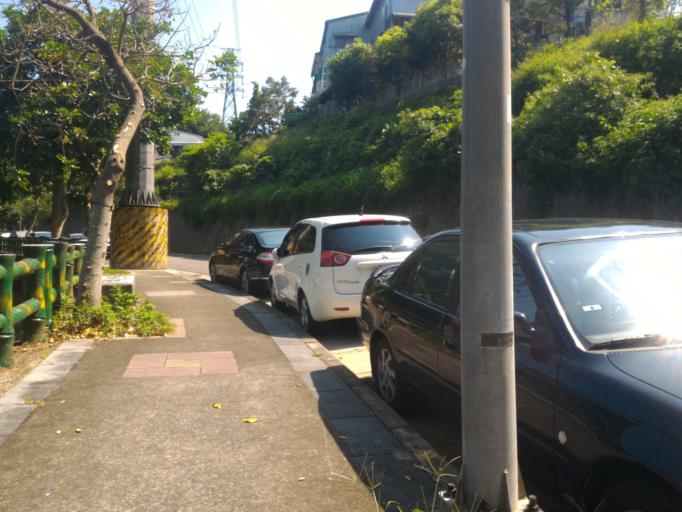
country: TW
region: Taipei
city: Taipei
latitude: 25.0378
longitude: 121.6156
